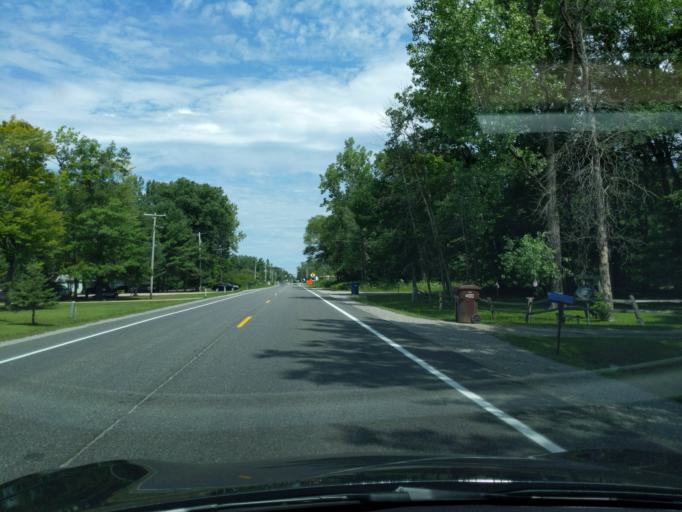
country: US
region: Michigan
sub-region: Midland County
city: Midland
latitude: 43.6086
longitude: -84.3692
